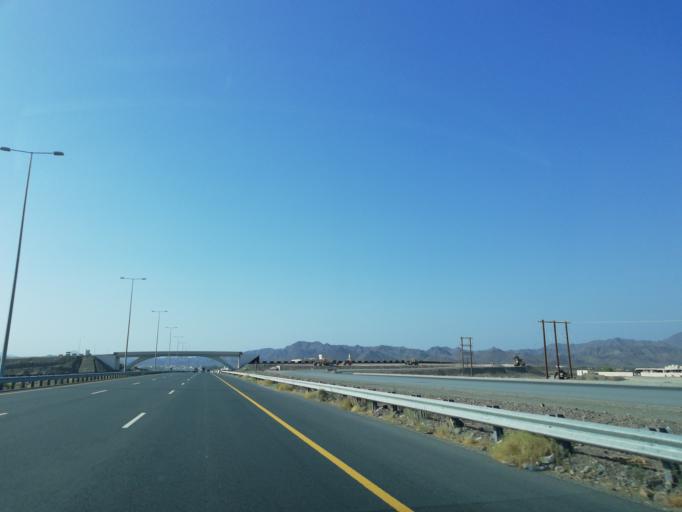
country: OM
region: Muhafazat ad Dakhiliyah
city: Sufalat Sama'il
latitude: 23.0433
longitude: 58.1980
